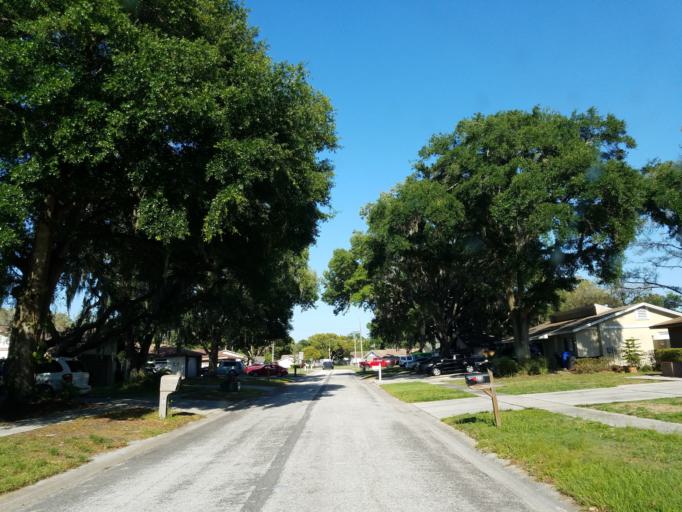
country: US
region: Florida
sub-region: Hillsborough County
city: Riverview
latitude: 27.8889
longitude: -82.2962
